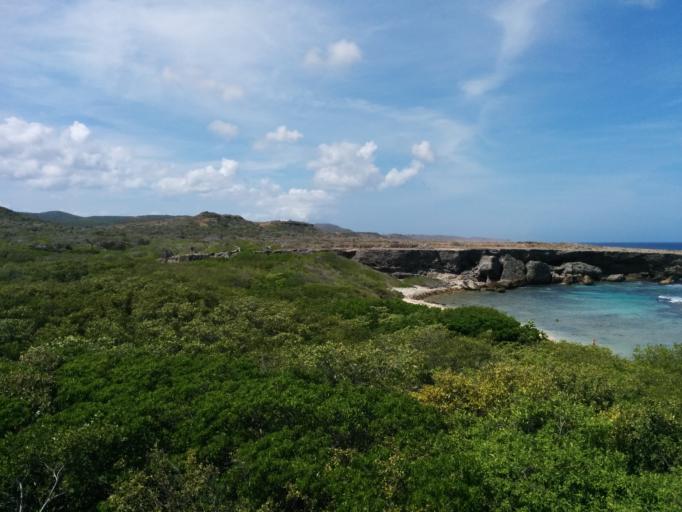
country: CW
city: Barber
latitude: 12.3583
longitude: -69.0962
